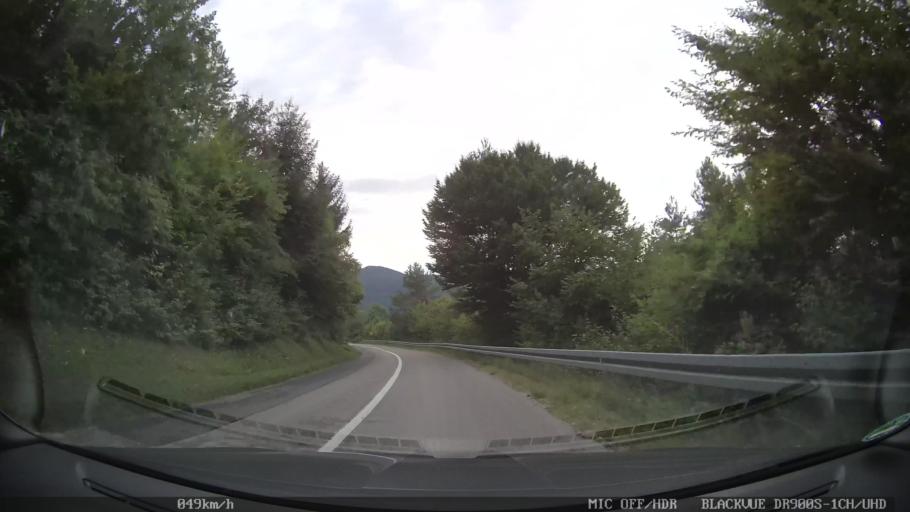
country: HR
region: Karlovacka
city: Plaski
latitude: 44.9934
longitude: 15.4517
